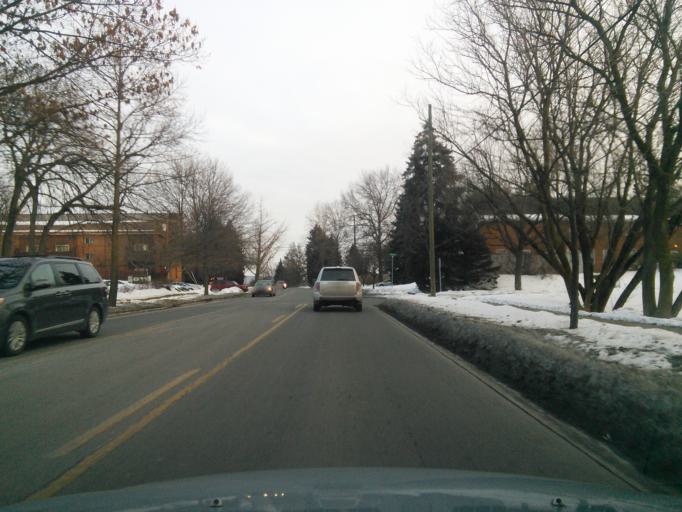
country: US
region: Pennsylvania
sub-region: Centre County
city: State College
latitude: 40.7989
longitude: -77.8475
